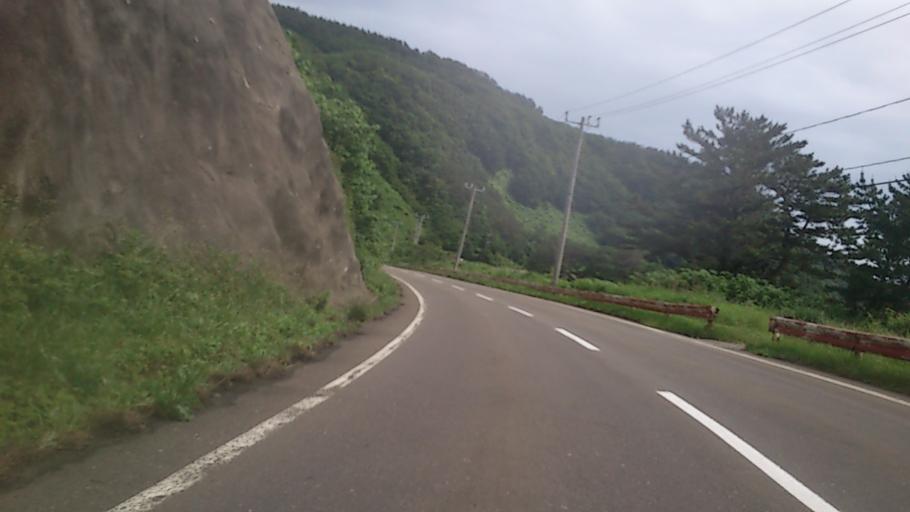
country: JP
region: Akita
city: Noshiromachi
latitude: 40.4674
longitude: 139.9449
